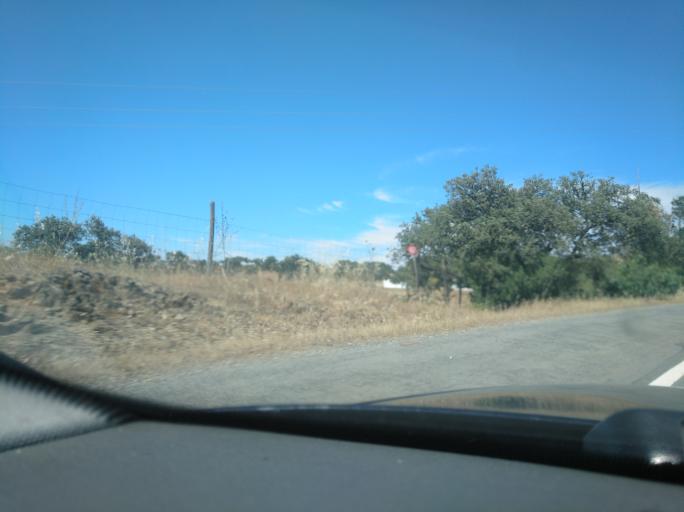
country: PT
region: Beja
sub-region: Almodovar
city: Almodovar
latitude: 37.5417
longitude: -7.9859
